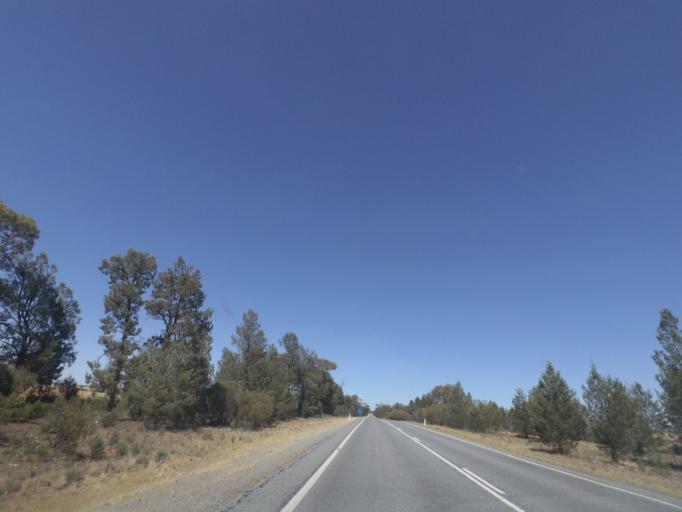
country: AU
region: New South Wales
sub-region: Narrandera
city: Narrandera
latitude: -34.4140
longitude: 146.8660
